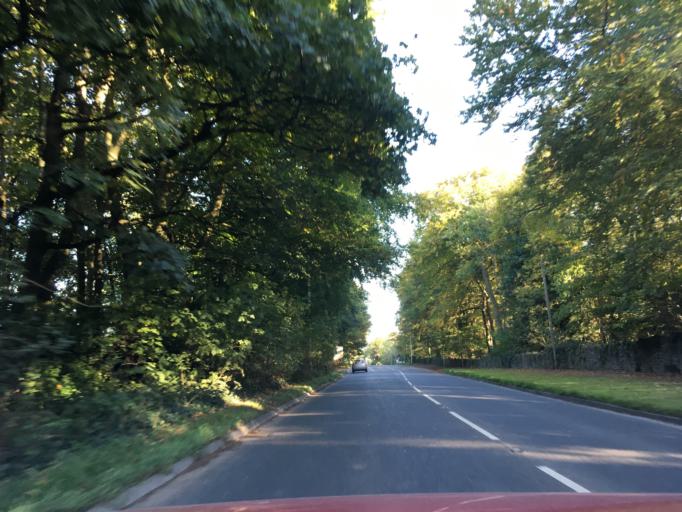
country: GB
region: England
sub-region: North Somerset
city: Long Ashton
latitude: 51.4565
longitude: -2.6486
